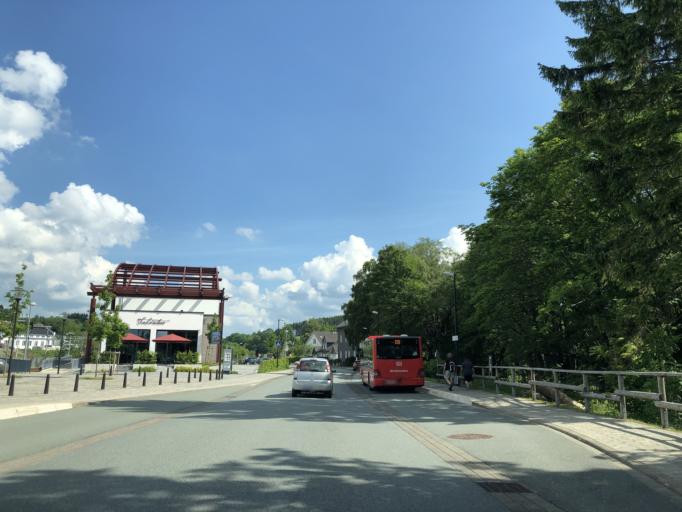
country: DE
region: North Rhine-Westphalia
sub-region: Regierungsbezirk Arnsberg
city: Winterberg
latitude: 51.1975
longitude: 8.5326
